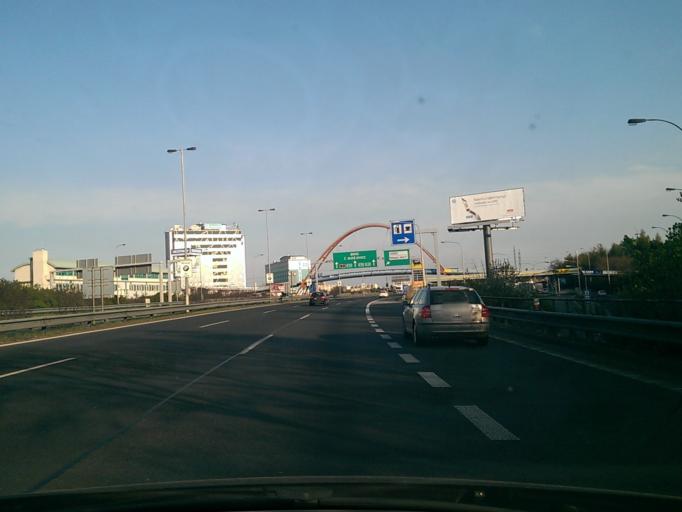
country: CZ
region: Central Bohemia
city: Vestec
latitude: 50.0387
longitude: 14.4880
